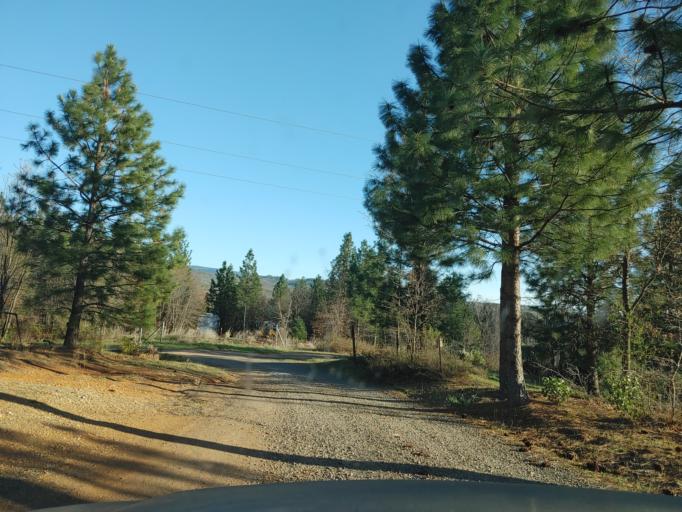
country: US
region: California
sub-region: Shasta County
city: Burney
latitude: 40.8089
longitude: -121.9418
